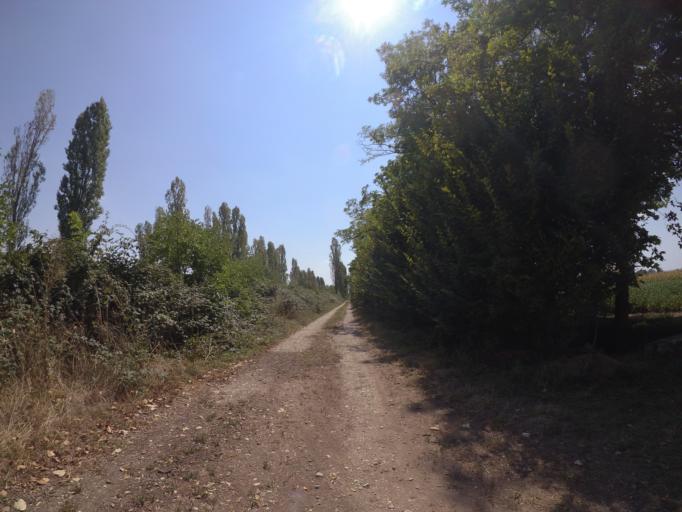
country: IT
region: Friuli Venezia Giulia
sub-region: Provincia di Udine
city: Codroipo
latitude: 45.9596
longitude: 13.0108
